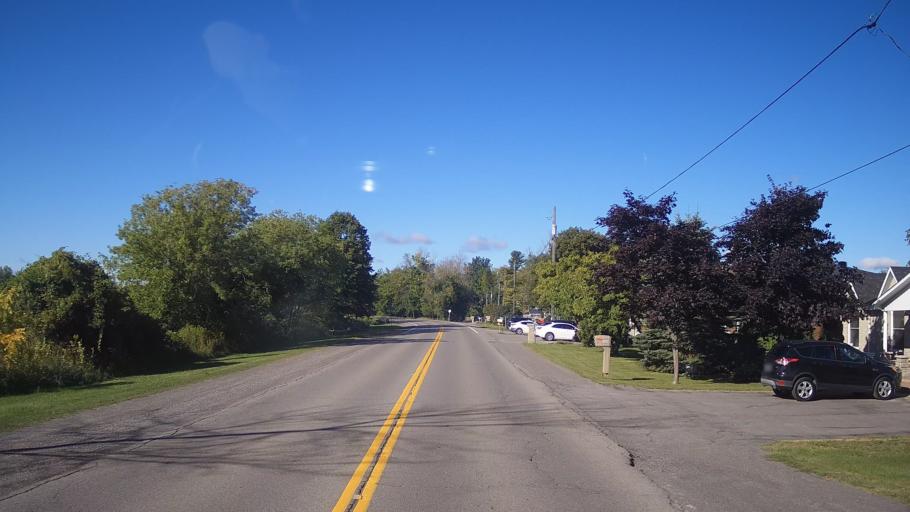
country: CA
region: Ontario
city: Bells Corners
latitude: 45.0920
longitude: -75.6247
